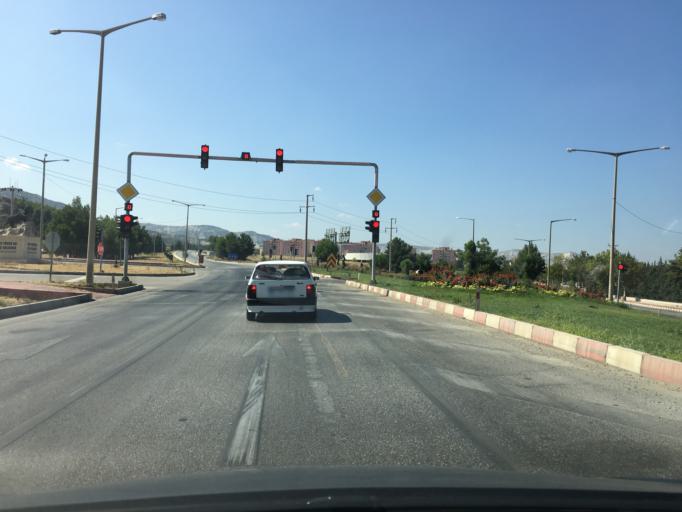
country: TR
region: Burdur
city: Burdur
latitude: 37.7413
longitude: 30.3128
